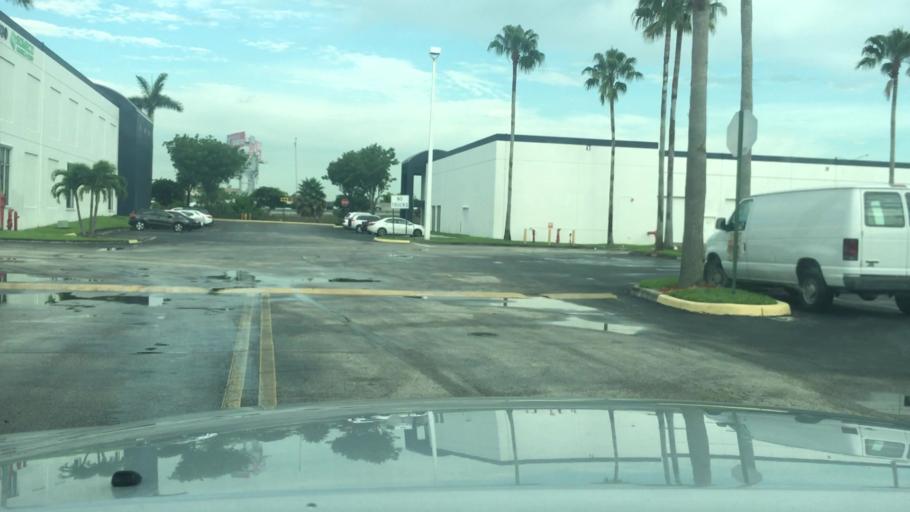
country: US
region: Florida
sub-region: Miami-Dade County
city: Virginia Gardens
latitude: 25.7942
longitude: -80.3196
